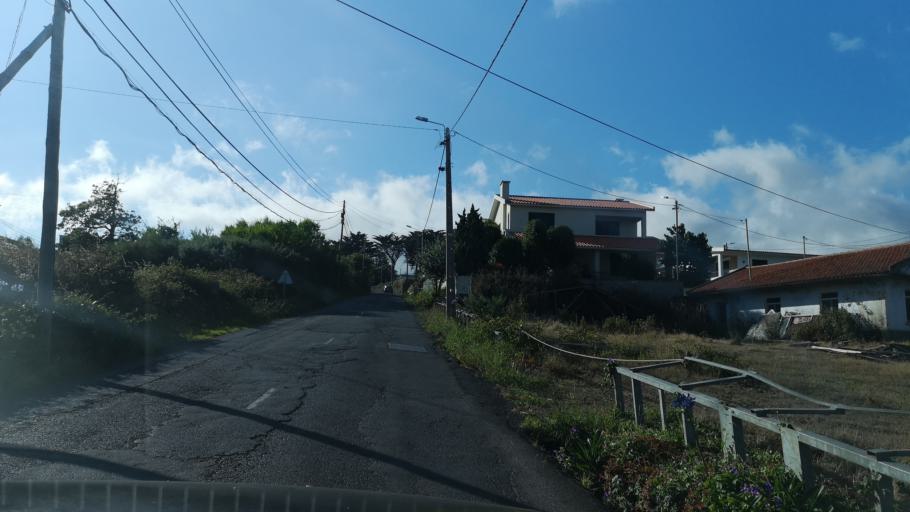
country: PT
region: Madeira
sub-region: Santa Cruz
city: Camacha
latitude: 32.6686
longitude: -16.8426
